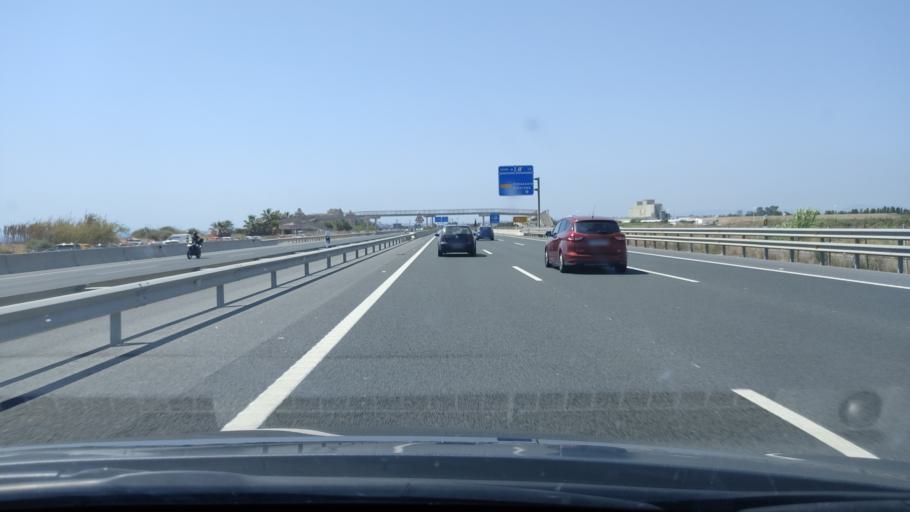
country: ES
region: Valencia
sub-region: Provincia de Valencia
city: Meliana
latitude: 39.5240
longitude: -0.3160
